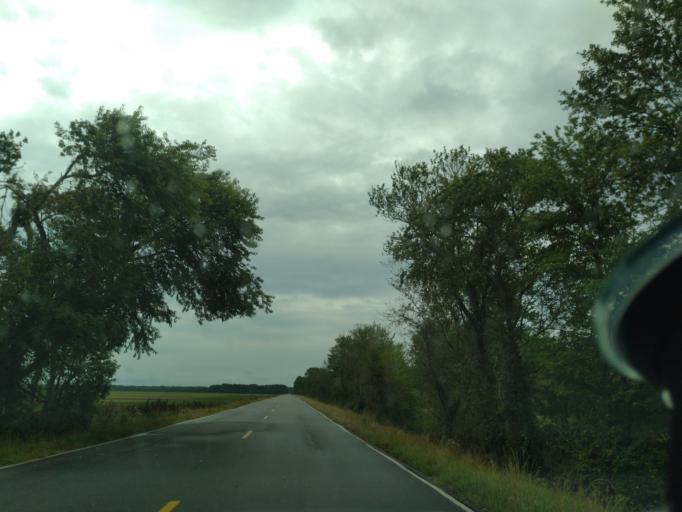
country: US
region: North Carolina
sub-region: Washington County
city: Plymouth
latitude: 35.8373
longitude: -76.5374
